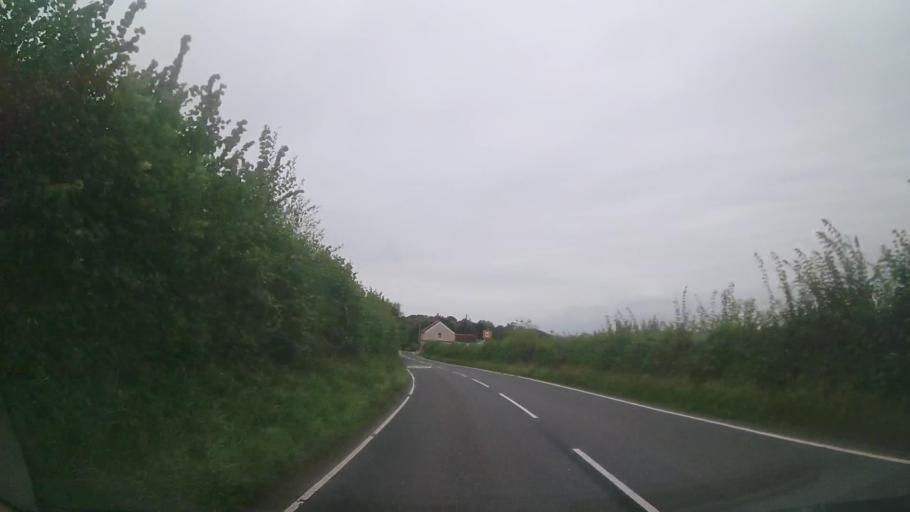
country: GB
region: Wales
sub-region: Carmarthenshire
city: Saint Clears
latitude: 51.8060
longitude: -4.4968
